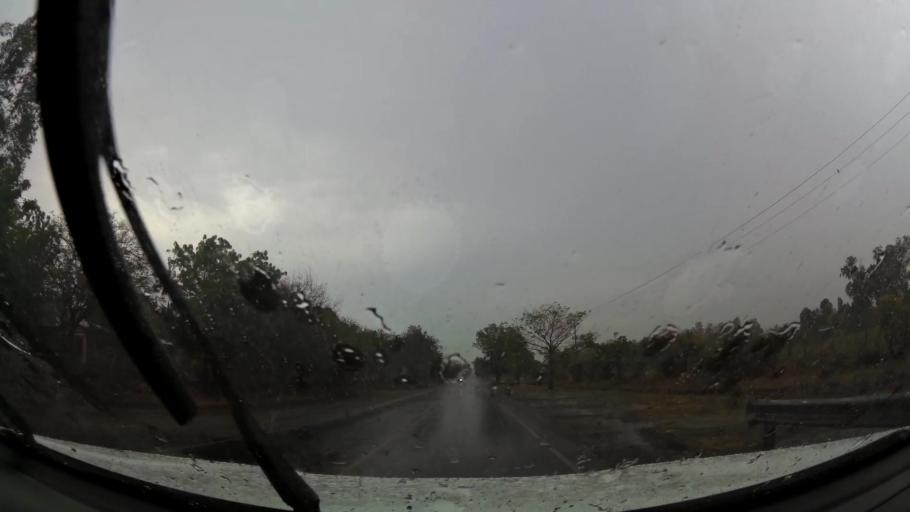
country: NI
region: Leon
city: Telica
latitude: 12.5288
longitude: -86.8567
